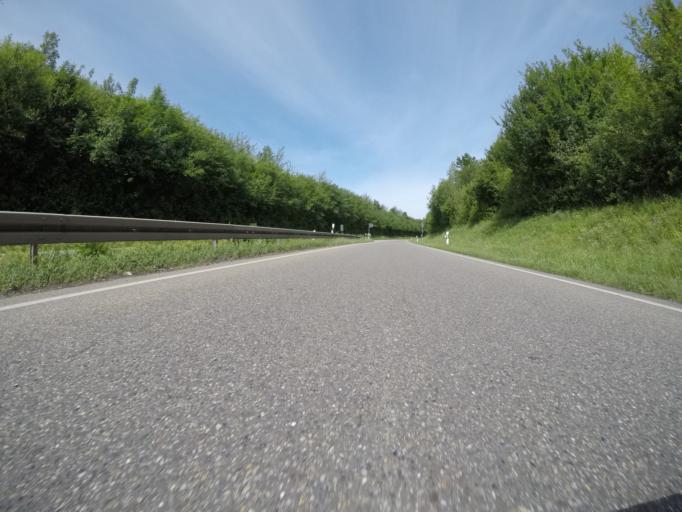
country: DE
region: Baden-Wuerttemberg
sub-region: Regierungsbezirk Stuttgart
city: Korntal
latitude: 48.8095
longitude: 9.1056
